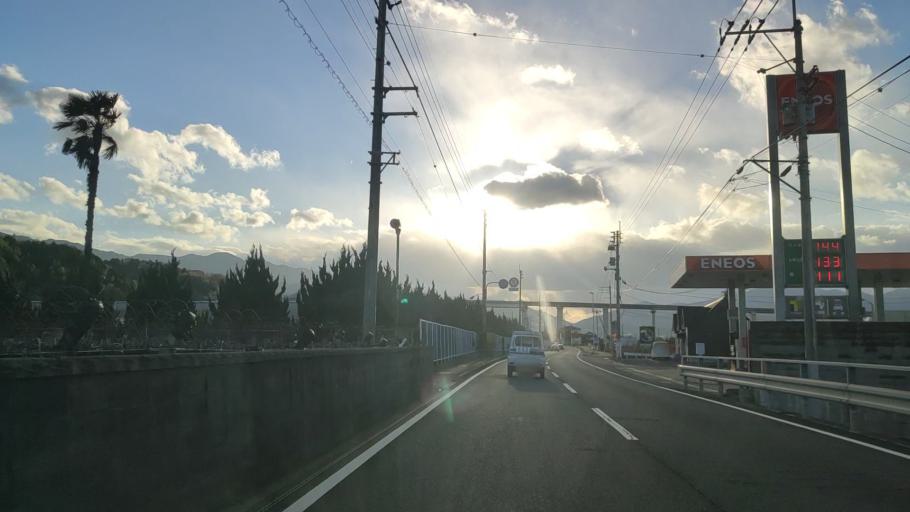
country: JP
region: Ehime
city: Saijo
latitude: 33.8918
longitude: 133.0902
